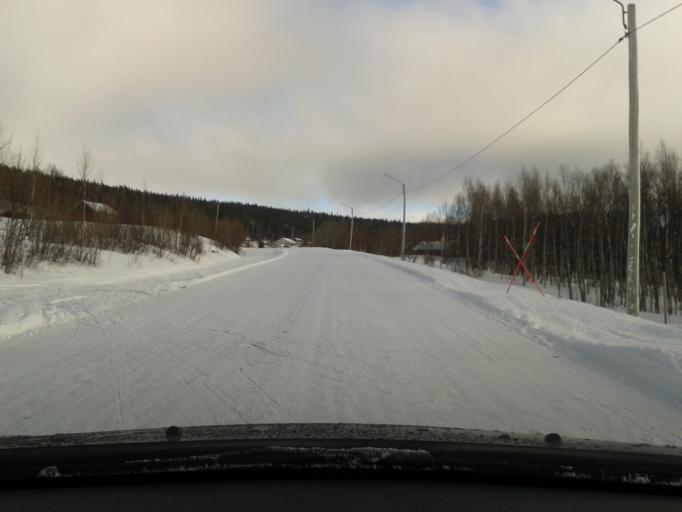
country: SE
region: Vaesterbotten
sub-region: Vilhelmina Kommun
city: Sjoberg
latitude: 65.2529
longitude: 15.5121
